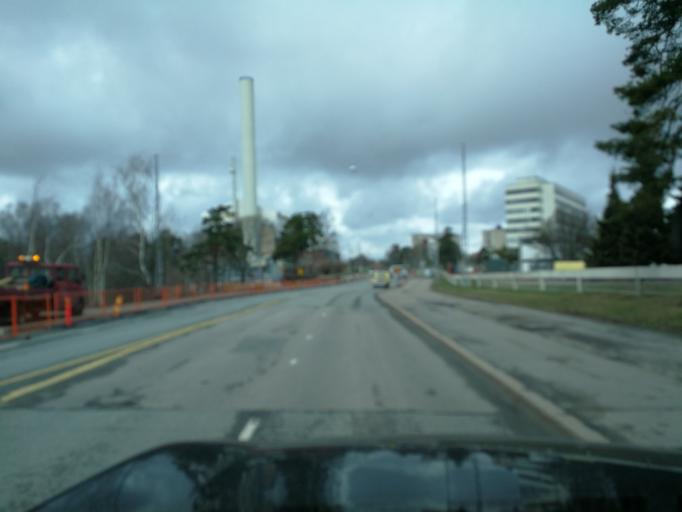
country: FI
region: Uusimaa
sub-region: Helsinki
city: Helsinki
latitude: 60.1875
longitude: 24.9046
